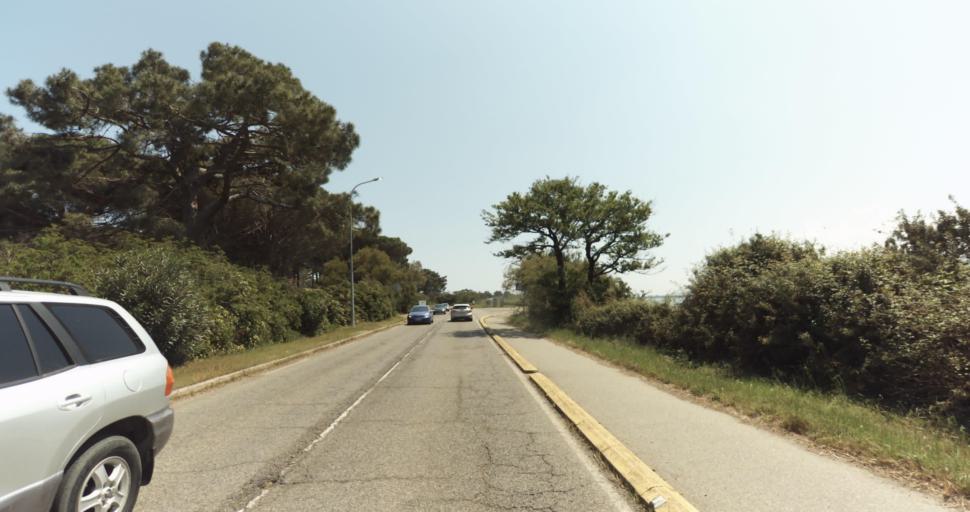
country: FR
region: Corsica
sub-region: Departement de la Haute-Corse
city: Biguglia
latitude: 42.6440
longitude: 9.4561
